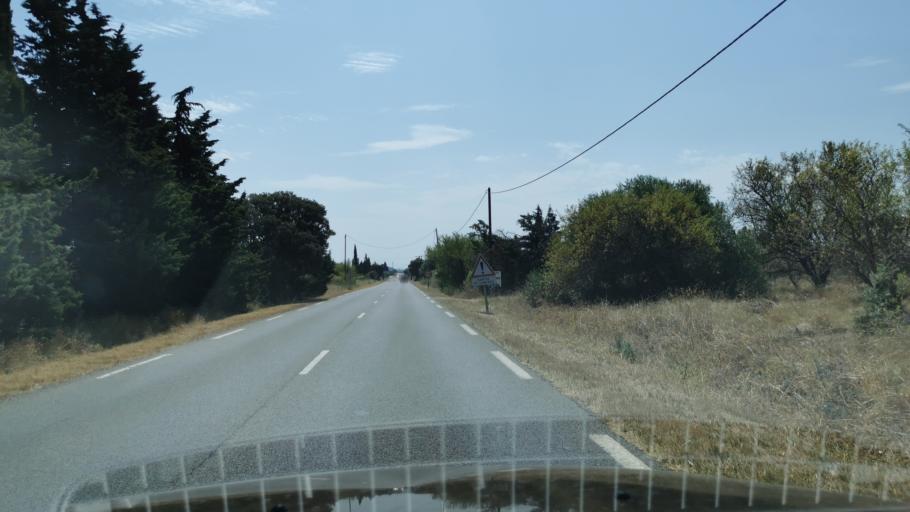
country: FR
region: Languedoc-Roussillon
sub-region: Departement de l'Aude
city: Ginestas
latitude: 43.2675
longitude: 2.8976
